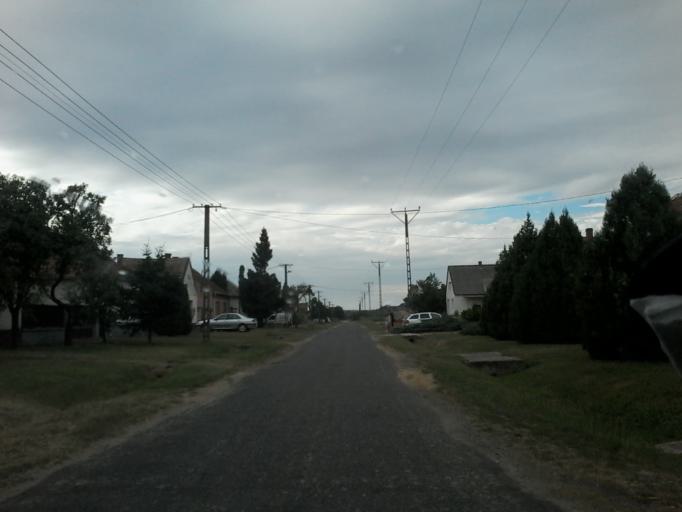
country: HU
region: Vas
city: Celldomolk
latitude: 47.2099
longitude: 17.0587
